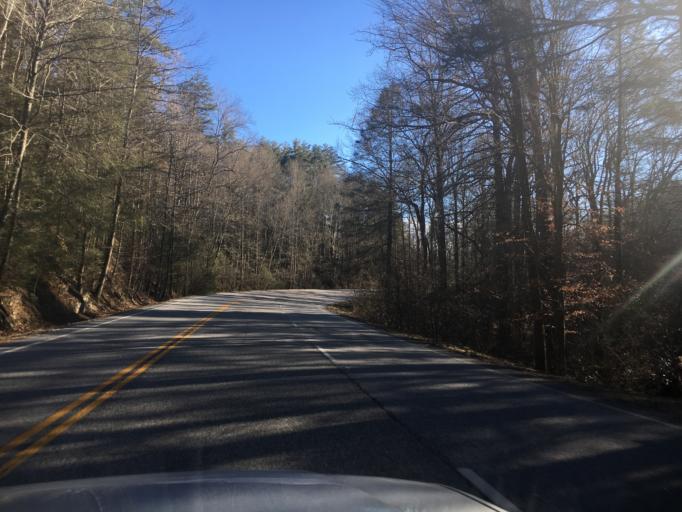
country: US
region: Georgia
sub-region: Lumpkin County
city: Dahlonega
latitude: 34.6948
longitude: -83.9128
